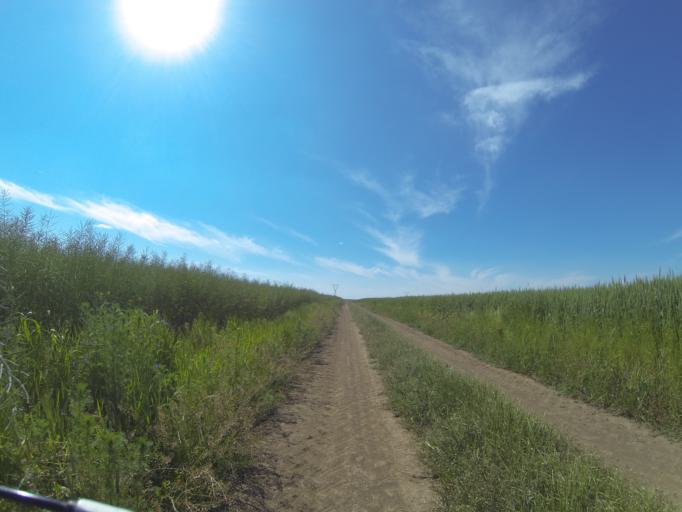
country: RO
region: Dolj
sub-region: Comuna Leu
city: Leu
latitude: 44.2563
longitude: 24.0082
